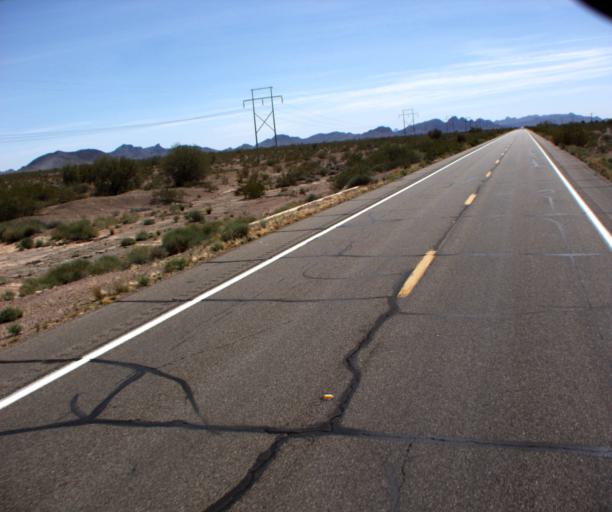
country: US
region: Arizona
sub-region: La Paz County
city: Quartzsite
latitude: 33.3926
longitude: -114.2172
